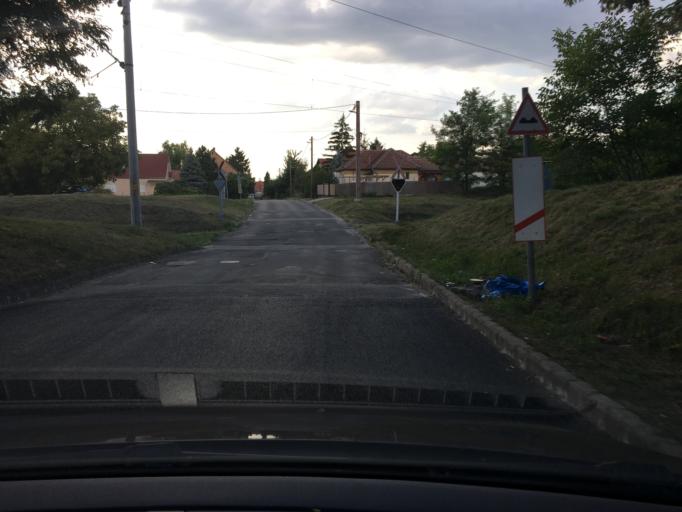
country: HU
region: Pest
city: Veresegyhaz
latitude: 47.6538
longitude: 19.2940
